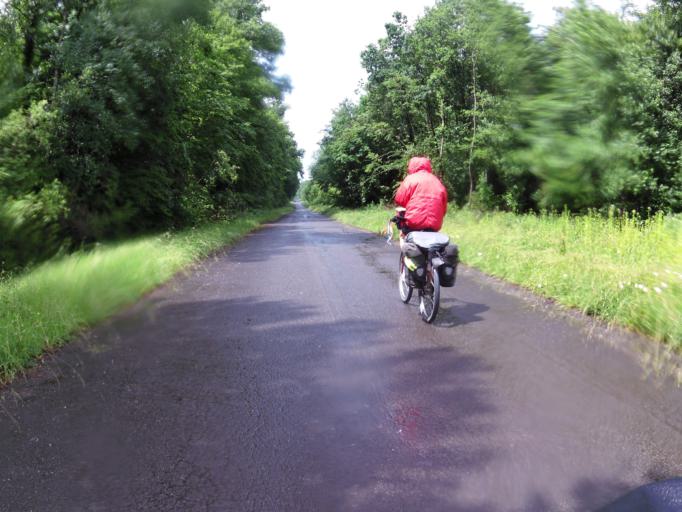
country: FR
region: Champagne-Ardenne
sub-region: Departement de la Marne
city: Sermaize-les-Bains
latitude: 48.7462
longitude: 4.9751
